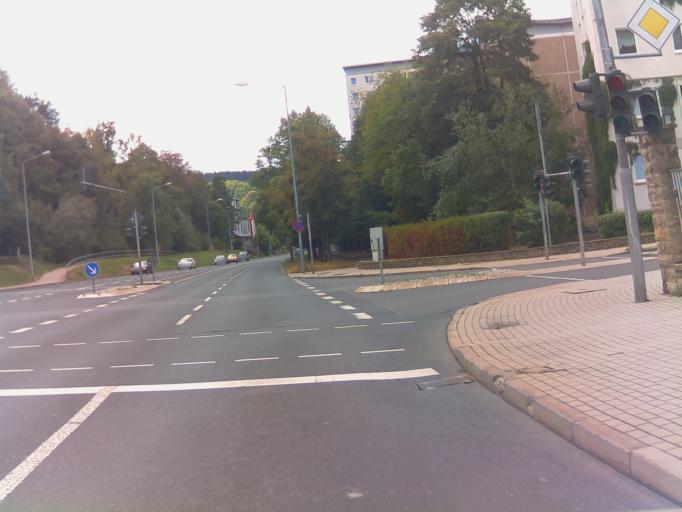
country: DE
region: Thuringia
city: Suhl
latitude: 50.6076
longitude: 10.6822
